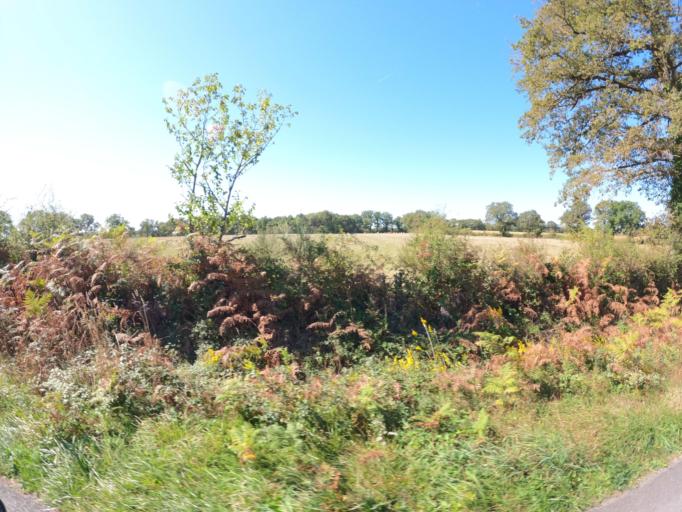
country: FR
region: Poitou-Charentes
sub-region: Departement de la Vienne
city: Lathus-Saint-Remy
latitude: 46.2934
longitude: 1.0003
